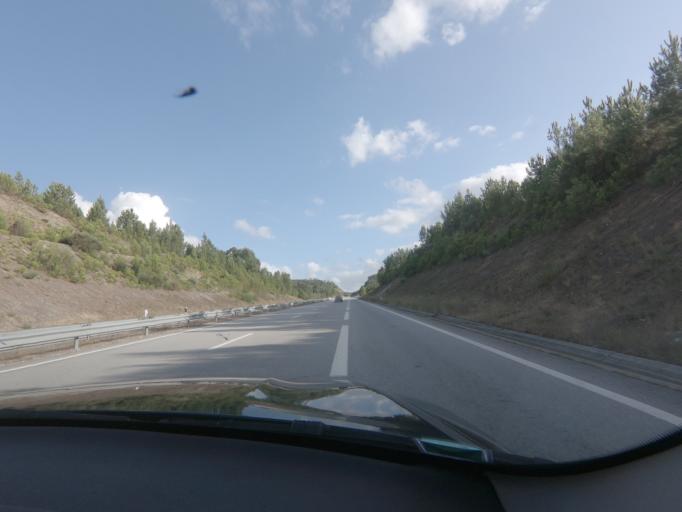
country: PT
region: Viseu
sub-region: Viseu
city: Campo
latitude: 40.7894
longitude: -7.9287
